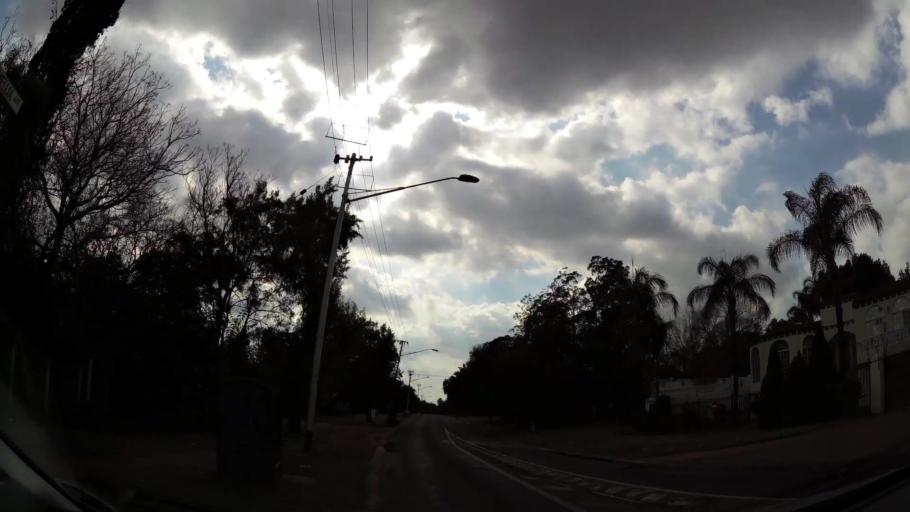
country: ZA
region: Gauteng
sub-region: City of Tshwane Metropolitan Municipality
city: Pretoria
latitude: -25.7649
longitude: 28.2893
